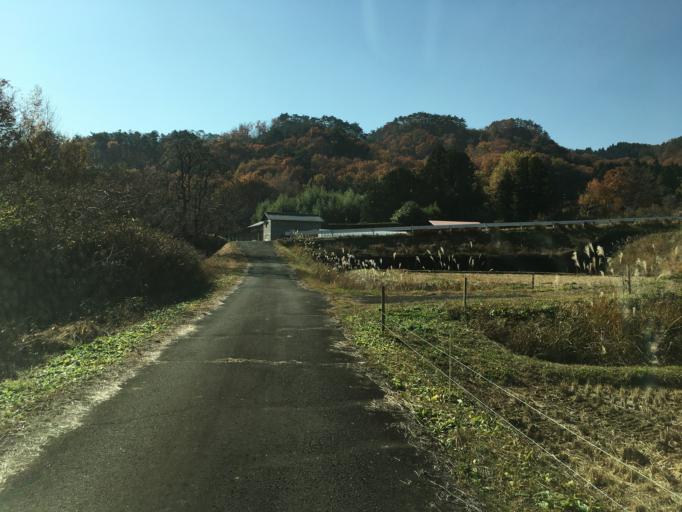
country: JP
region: Fukushima
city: Nihommatsu
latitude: 37.5749
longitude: 140.3725
